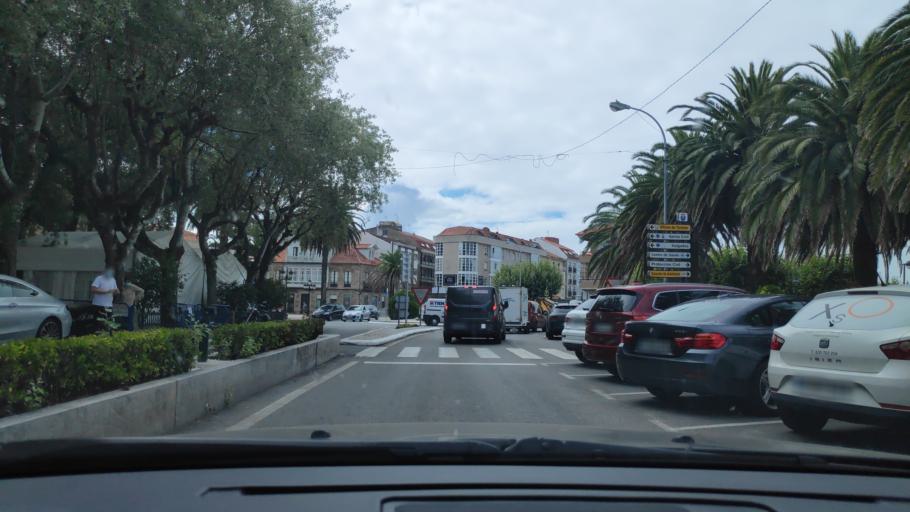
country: ES
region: Galicia
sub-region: Provincia de Pontevedra
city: Cambados
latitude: 42.5160
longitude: -8.8150
